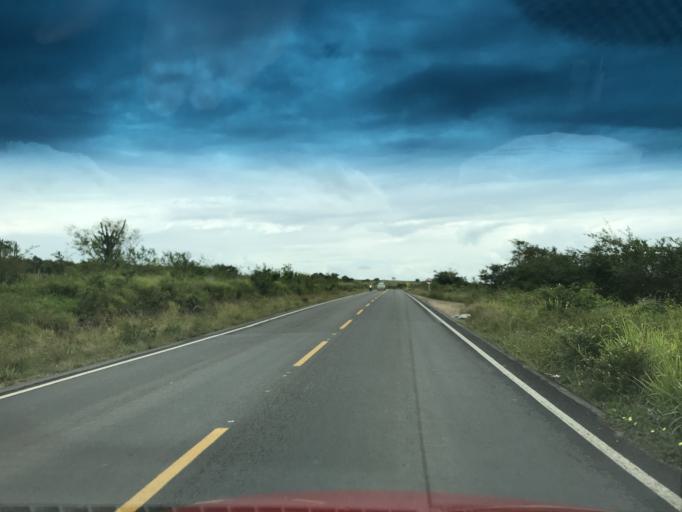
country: BR
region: Bahia
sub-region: Castro Alves
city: Castro Alves
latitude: -12.7546
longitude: -39.4102
